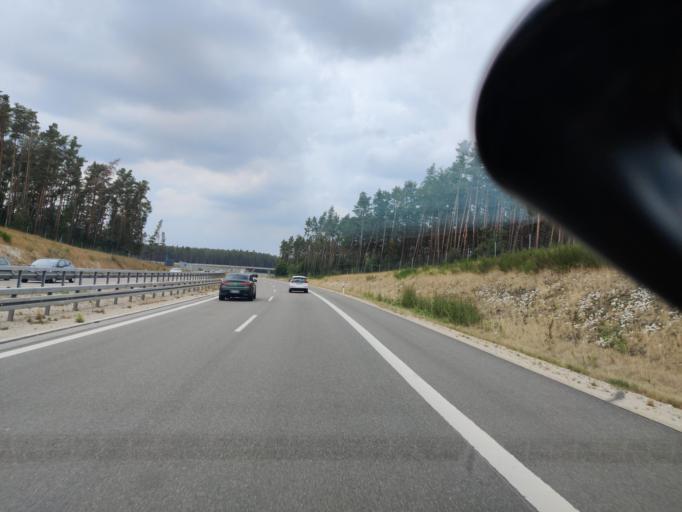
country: DE
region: Bavaria
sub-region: Regierungsbezirk Mittelfranken
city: Rottenbach
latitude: 49.1854
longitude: 11.0791
